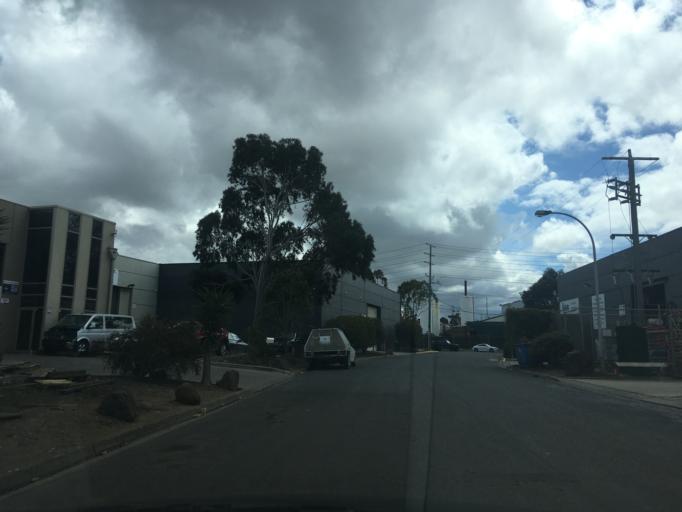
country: AU
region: Victoria
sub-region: Hobsons Bay
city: Laverton
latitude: -37.8388
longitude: 144.7851
